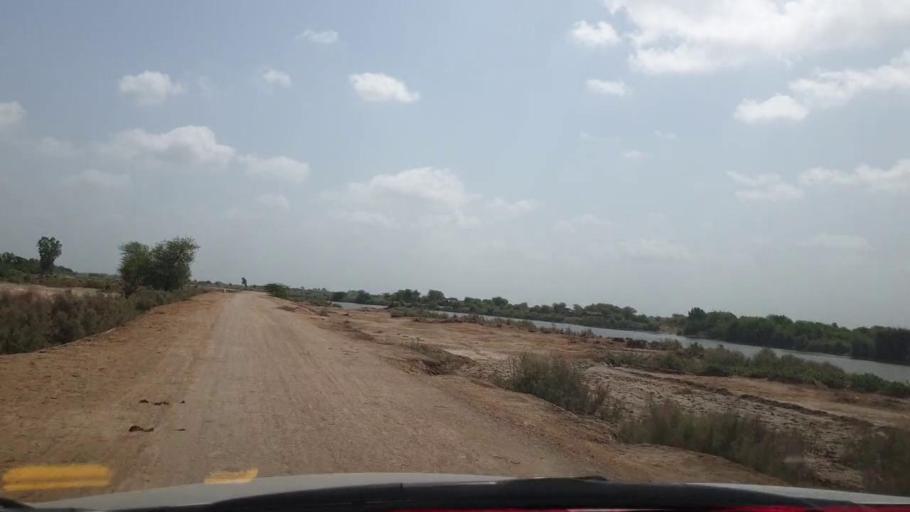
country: PK
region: Sindh
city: Talhar
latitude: 24.8792
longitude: 68.9100
